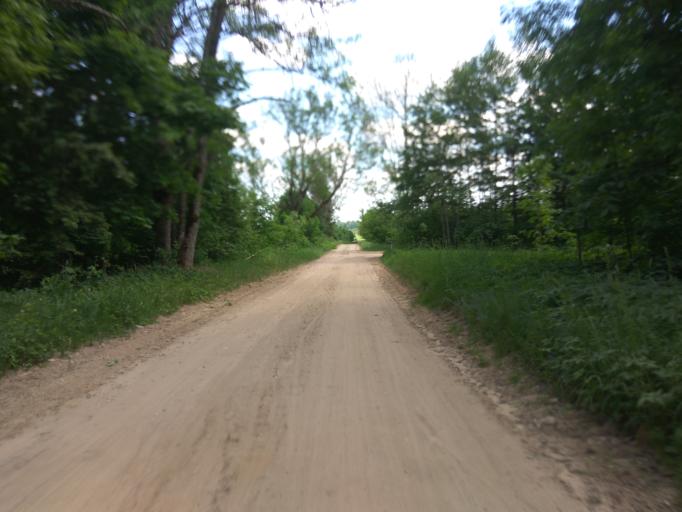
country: LV
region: Kuldigas Rajons
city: Kuldiga
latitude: 56.8908
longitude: 21.9724
